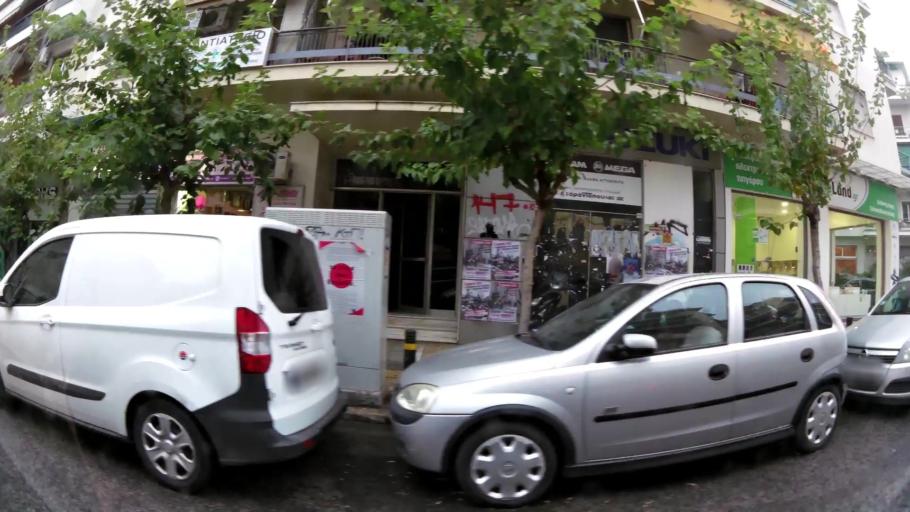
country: GR
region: Attica
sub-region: Nomarchia Athinas
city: Vyronas
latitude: 37.9711
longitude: 23.7474
